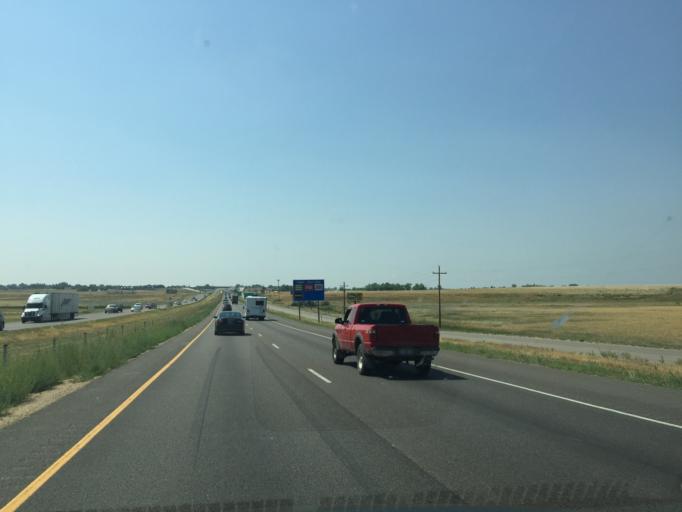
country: US
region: Colorado
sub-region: Weld County
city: Windsor
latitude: 40.4937
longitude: -104.9919
